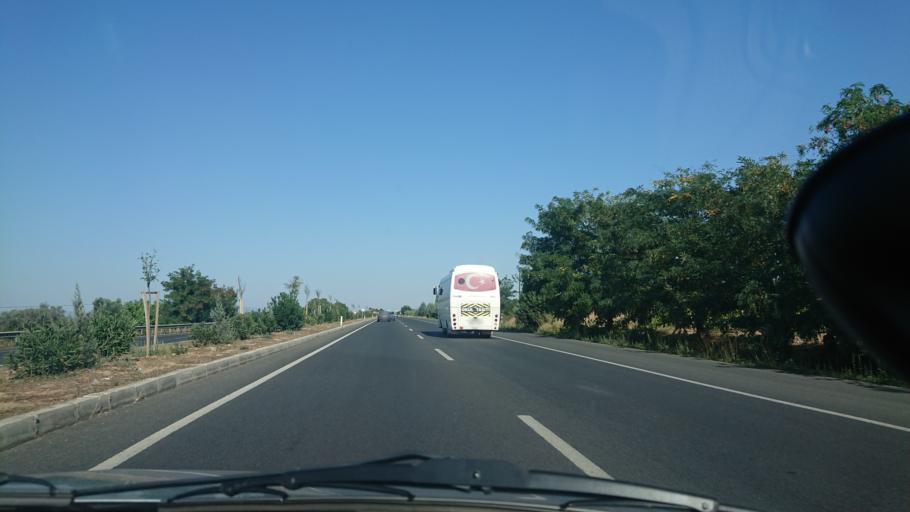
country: TR
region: Manisa
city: Ahmetli
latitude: 38.5058
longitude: 27.8869
